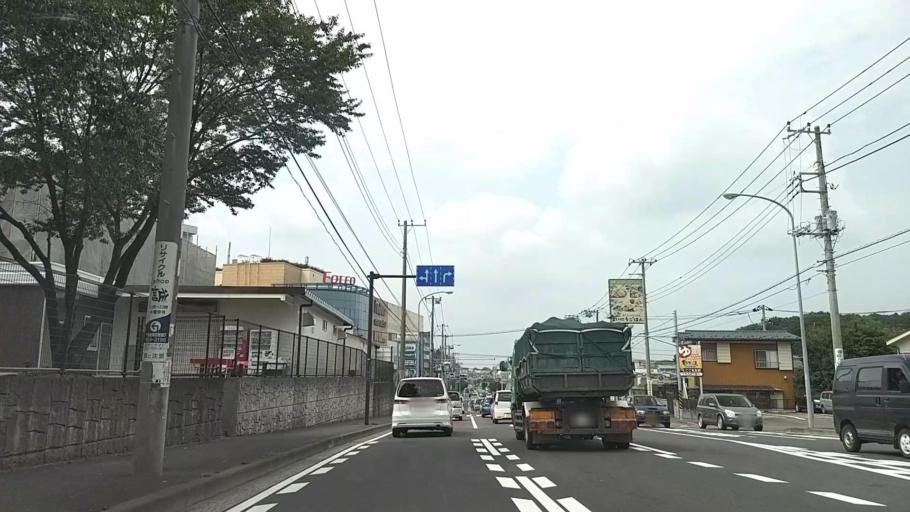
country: JP
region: Kanagawa
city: Minami-rinkan
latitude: 35.5007
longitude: 139.5415
